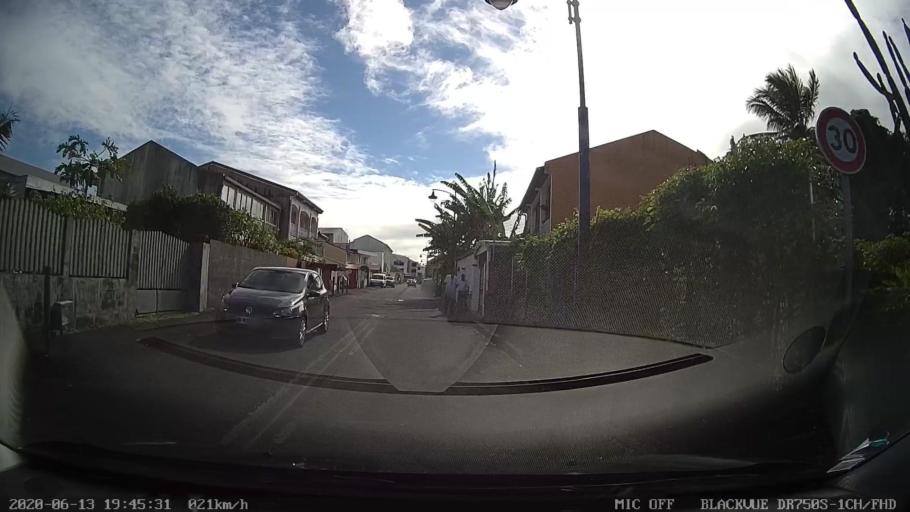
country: RE
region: Reunion
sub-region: Reunion
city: Bras-Panon
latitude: -20.9971
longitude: 55.6770
